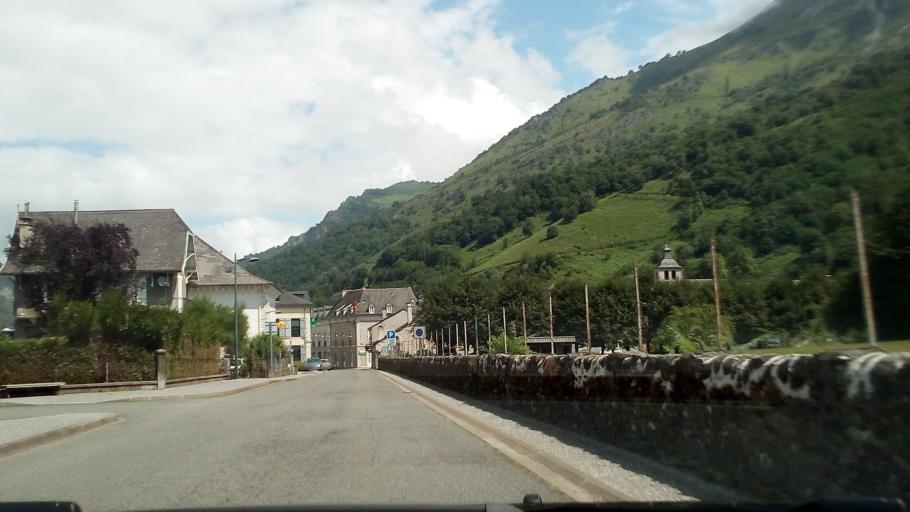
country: FR
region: Aquitaine
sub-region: Departement des Pyrenees-Atlantiques
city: Arette
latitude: 42.9971
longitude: -0.6013
